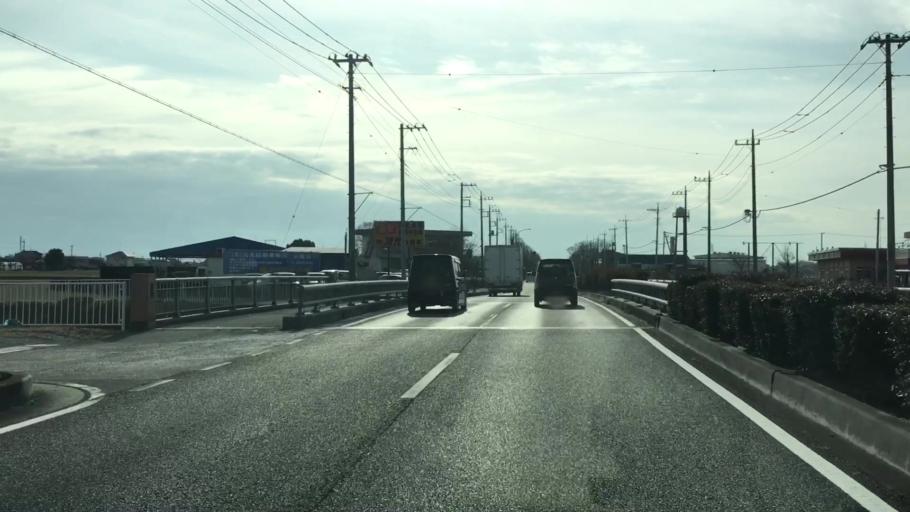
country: JP
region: Saitama
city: Menuma
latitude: 36.1997
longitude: 139.3705
